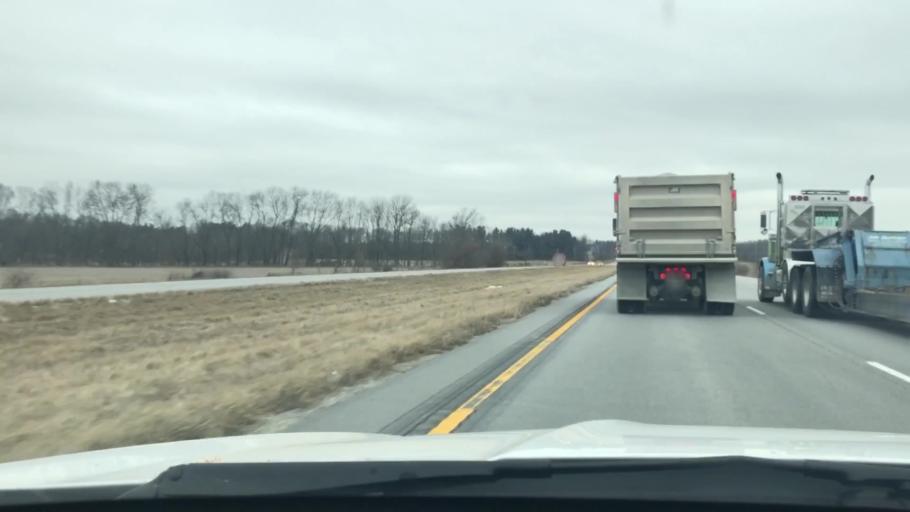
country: US
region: Indiana
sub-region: Miami County
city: Peru
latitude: 40.8257
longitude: -86.1292
